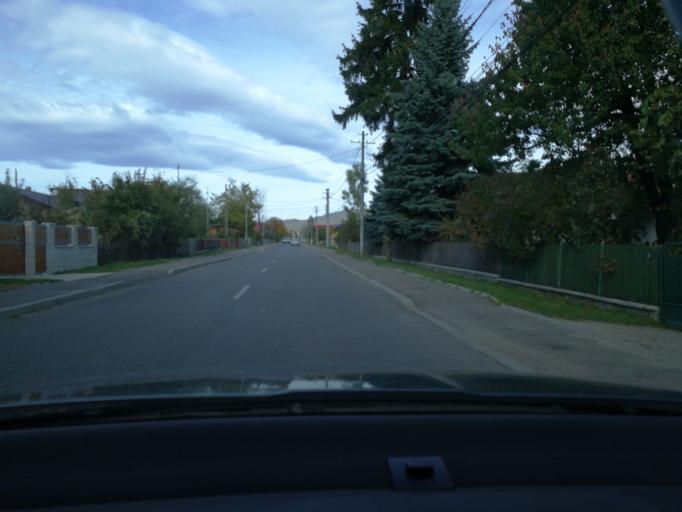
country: RO
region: Prahova
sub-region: Comuna Brebu
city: Brebu Megiesesc
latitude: 45.1722
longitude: 25.7712
